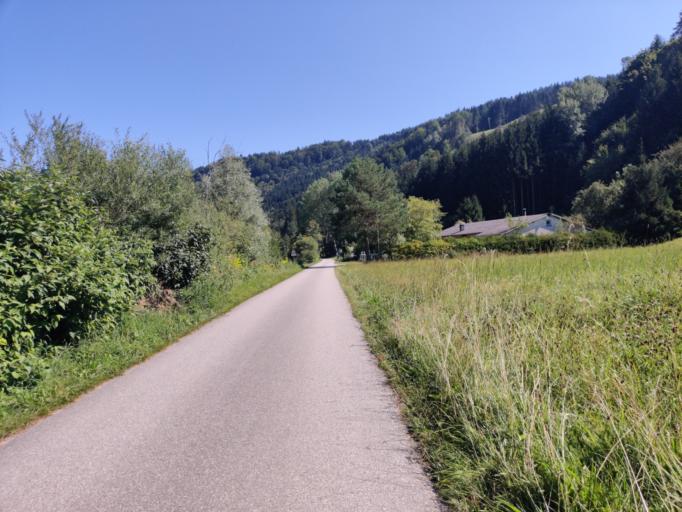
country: AT
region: Upper Austria
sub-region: Politischer Bezirk Rohrbach
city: Pfarrkirchen im Muehlkreis
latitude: 48.4475
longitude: 13.8672
